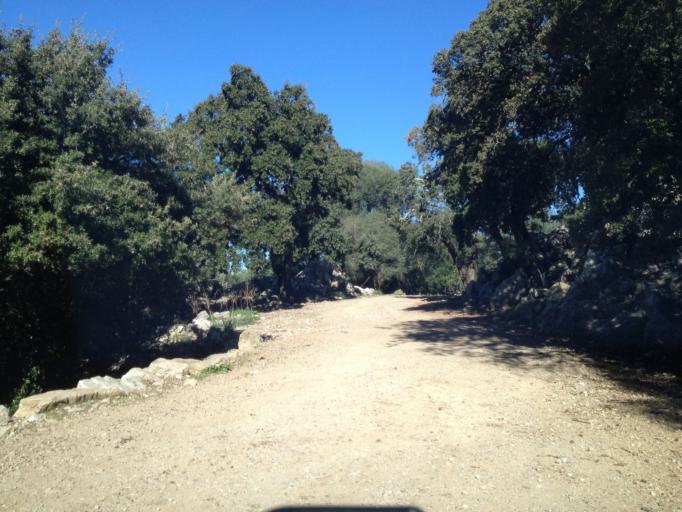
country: ES
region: Balearic Islands
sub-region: Illes Balears
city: Escorca
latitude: 39.8690
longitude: 2.9228
